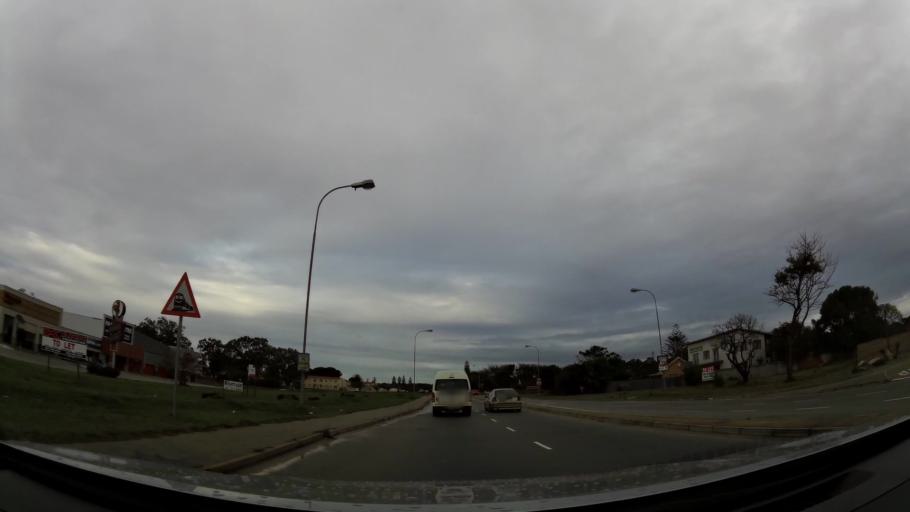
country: ZA
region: Eastern Cape
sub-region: Nelson Mandela Bay Metropolitan Municipality
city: Port Elizabeth
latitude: -33.9847
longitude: 25.5530
